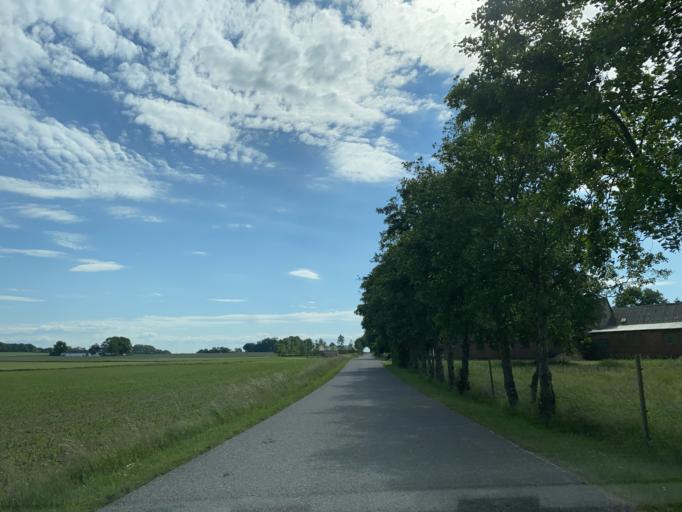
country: DK
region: Central Jutland
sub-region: Favrskov Kommune
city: Hammel
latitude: 56.2075
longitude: 9.8799
